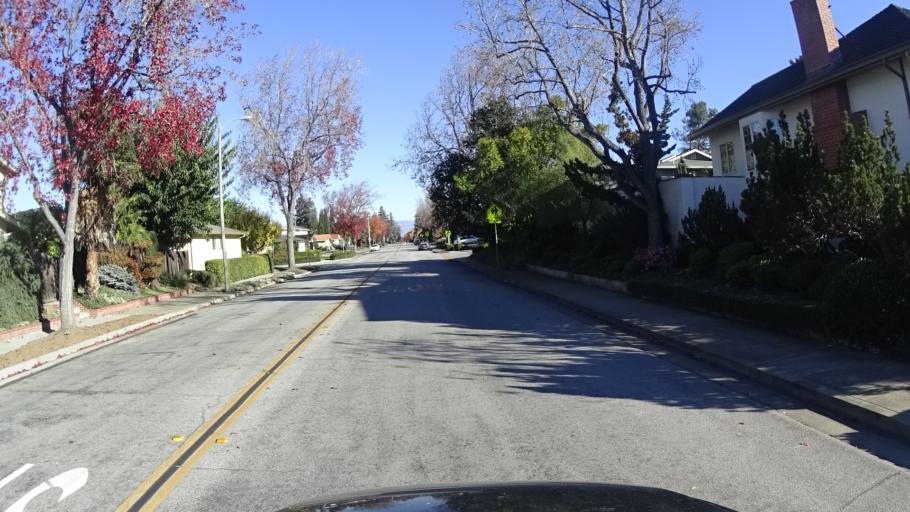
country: US
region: California
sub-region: Santa Clara County
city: Cupertino
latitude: 37.3411
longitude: -122.0301
